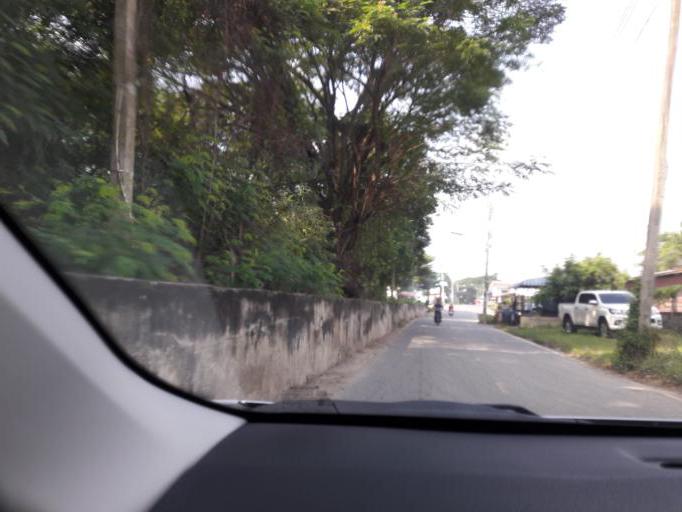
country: TH
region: Ang Thong
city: Ang Thong
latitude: 14.5897
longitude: 100.4494
